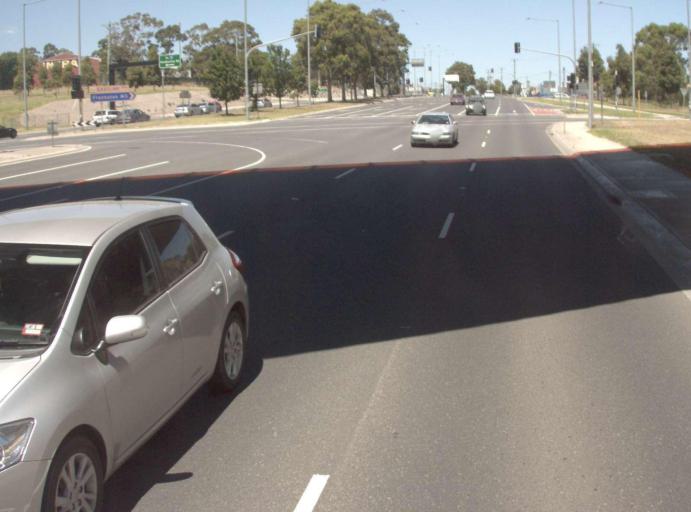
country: AU
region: Victoria
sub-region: Greater Dandenong
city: Dandenong North
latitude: -37.9676
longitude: 145.1948
